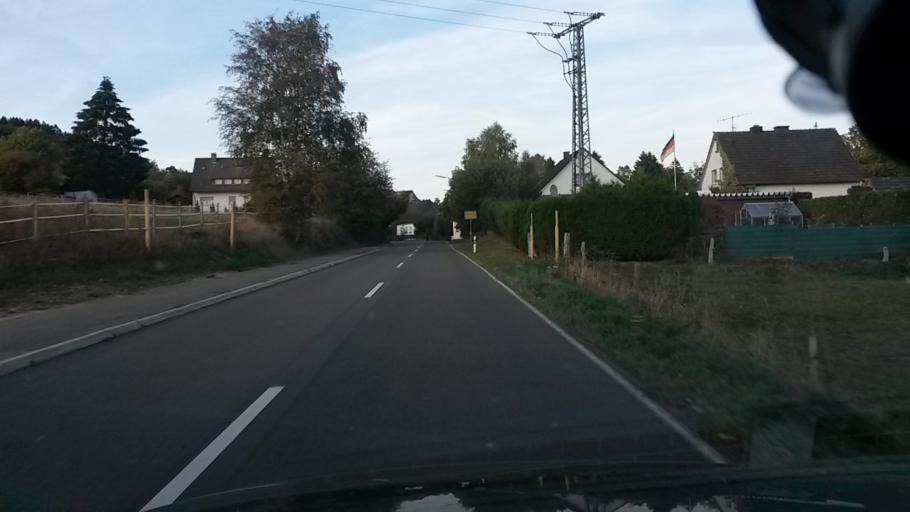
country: DE
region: North Rhine-Westphalia
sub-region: Regierungsbezirk Koln
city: Marienheide
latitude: 51.0737
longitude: 7.5197
